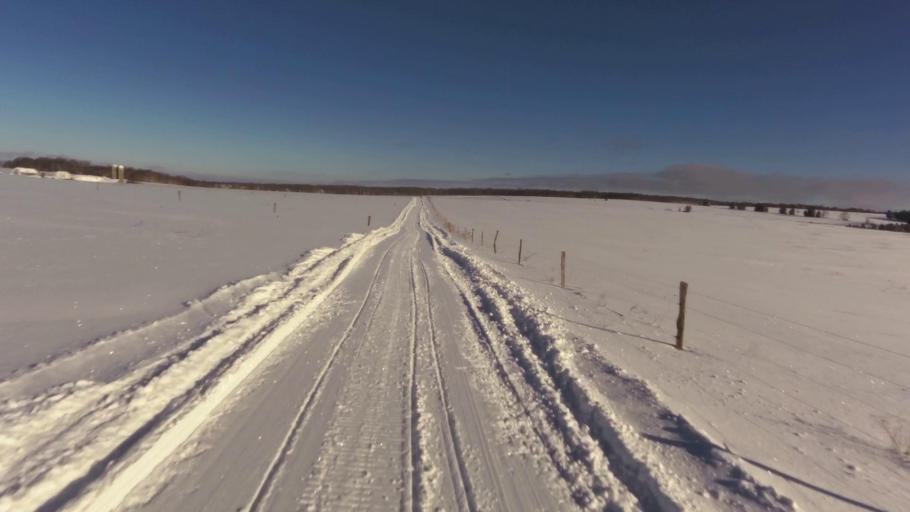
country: US
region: New York
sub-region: Chautauqua County
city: Falconer
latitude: 42.2558
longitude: -79.2028
